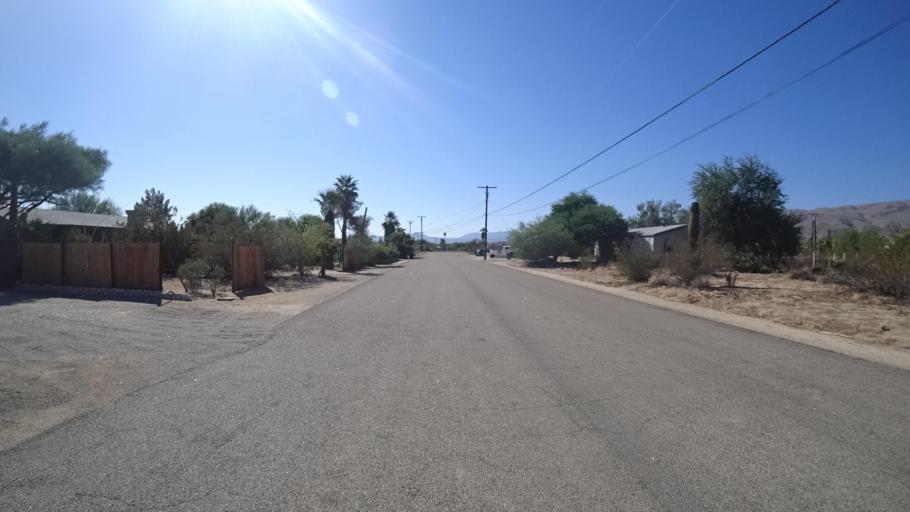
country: US
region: California
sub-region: San Diego County
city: Borrego Springs
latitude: 33.2743
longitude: -116.3926
